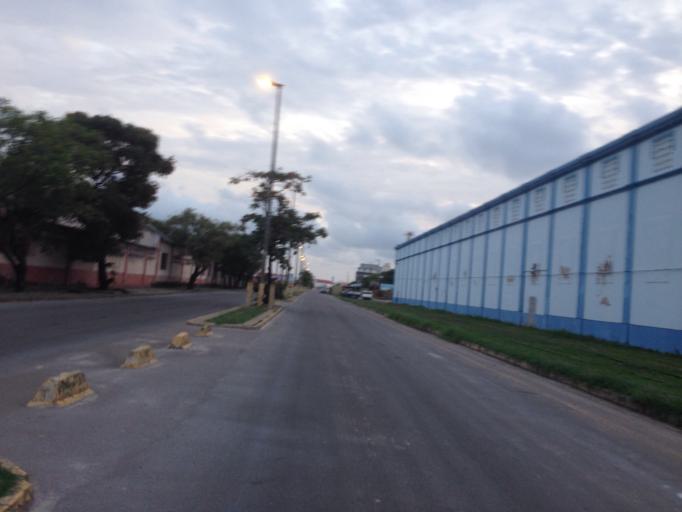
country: BR
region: Pernambuco
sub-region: Recife
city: Recife
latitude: -8.0513
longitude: -34.8698
